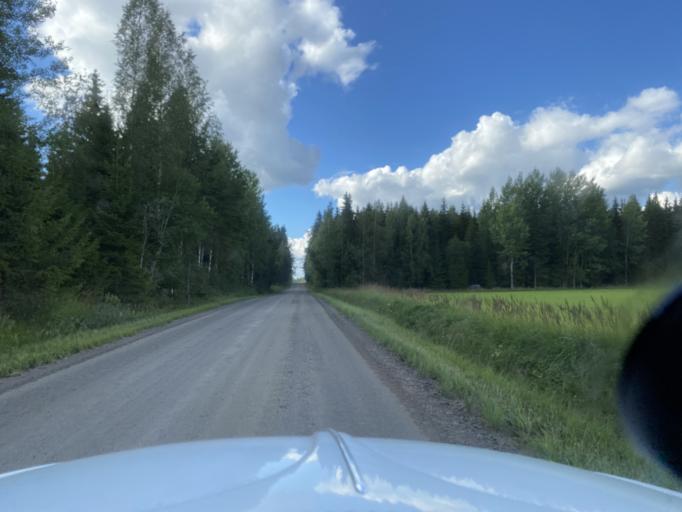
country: FI
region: Pirkanmaa
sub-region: Lounais-Pirkanmaa
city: Punkalaidun
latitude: 61.1177
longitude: 23.2715
